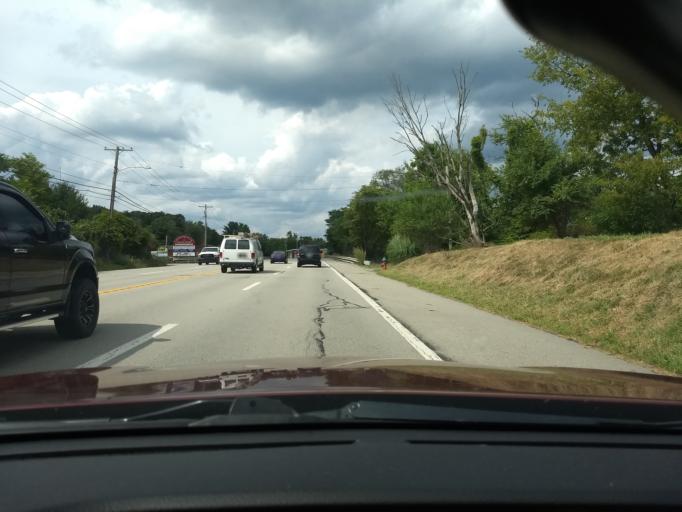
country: US
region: Pennsylvania
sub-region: Armstrong County
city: Freeport
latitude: 40.6535
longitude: -79.7077
